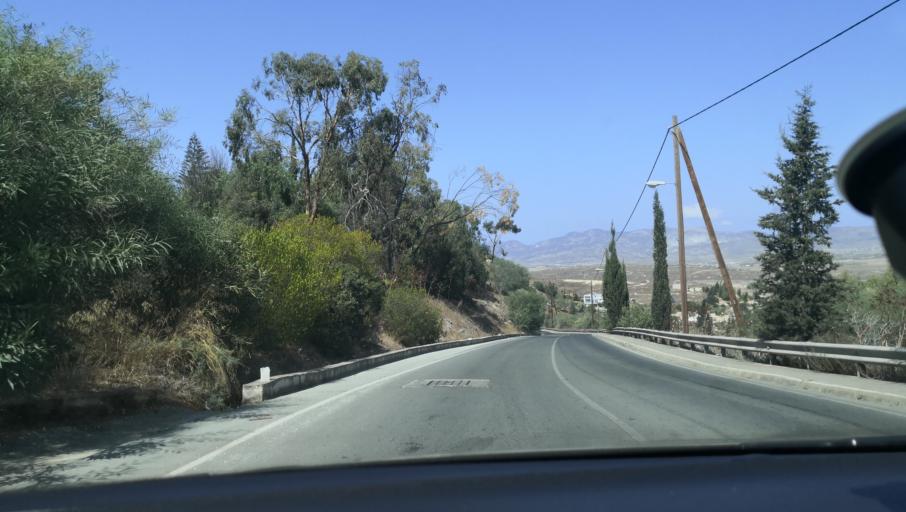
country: CY
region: Lefkosia
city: Mammari
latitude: 35.1686
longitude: 33.2026
